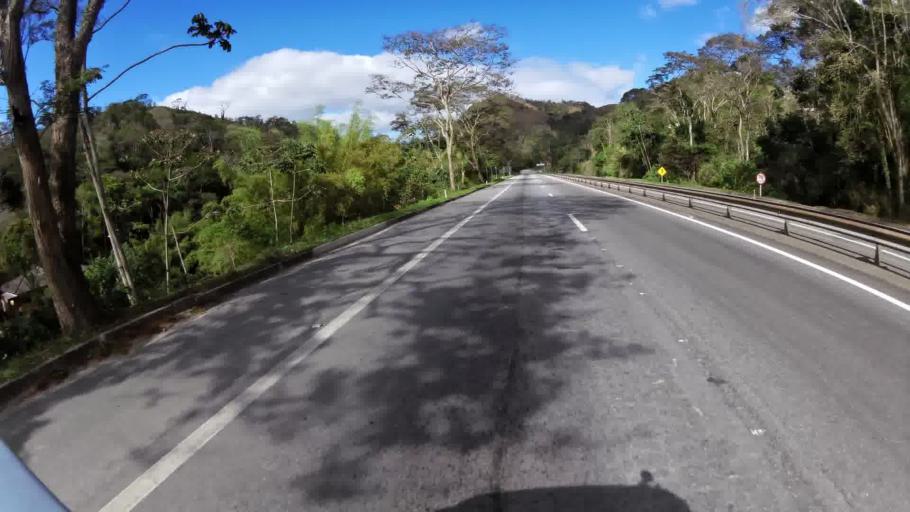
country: BR
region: Rio de Janeiro
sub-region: Areal
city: Areal
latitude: -22.2886
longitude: -43.1238
